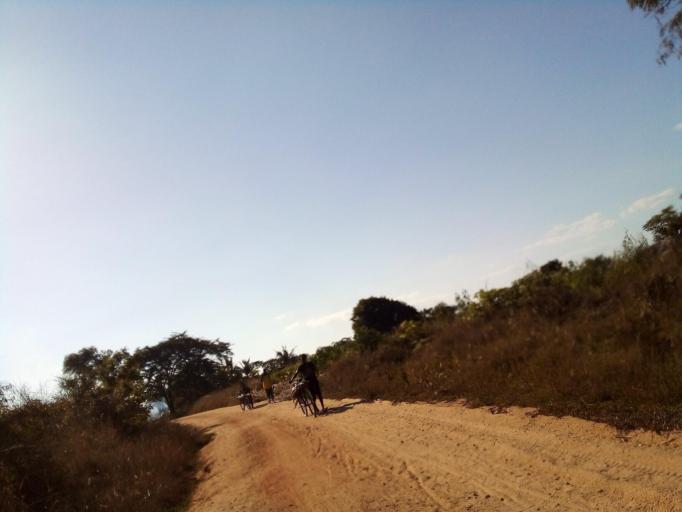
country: MZ
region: Zambezia
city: Quelimane
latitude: -17.4932
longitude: 36.5685
